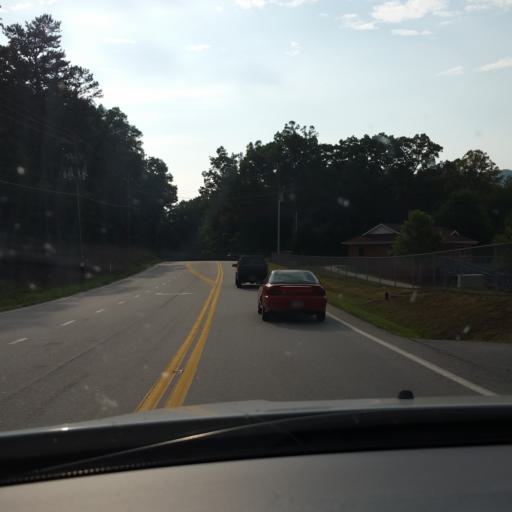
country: US
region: North Carolina
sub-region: Buncombe County
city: Bent Creek
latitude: 35.5328
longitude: -82.6636
